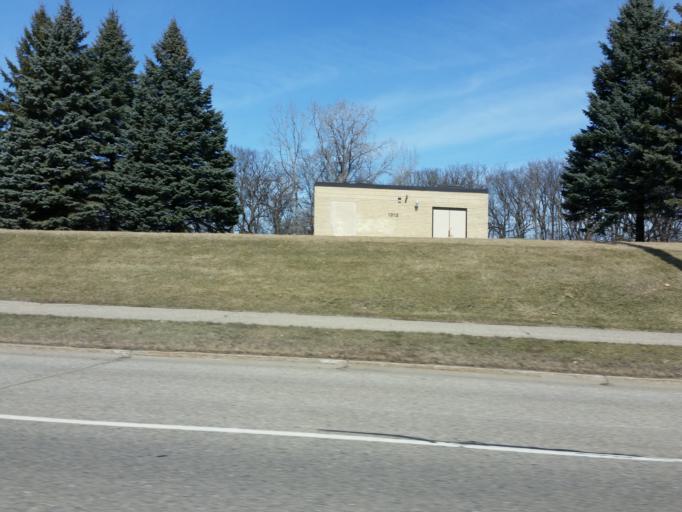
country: US
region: Minnesota
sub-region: Dakota County
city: Eagan
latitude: 44.7902
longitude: -93.1608
